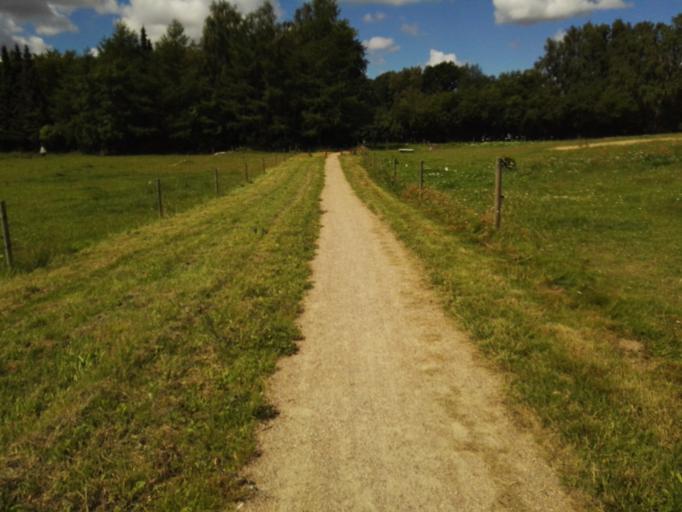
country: DK
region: Capital Region
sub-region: Ballerup Kommune
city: Ballerup
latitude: 55.7515
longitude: 12.3525
